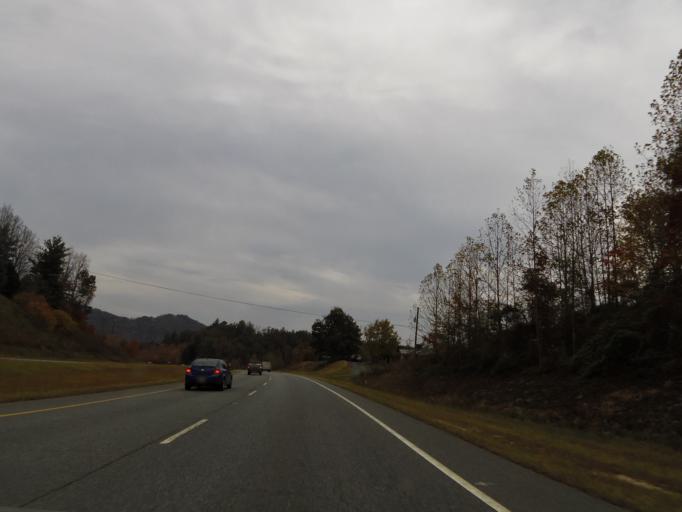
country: US
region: North Carolina
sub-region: Caldwell County
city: Lenoir
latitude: 35.9896
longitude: -81.5724
